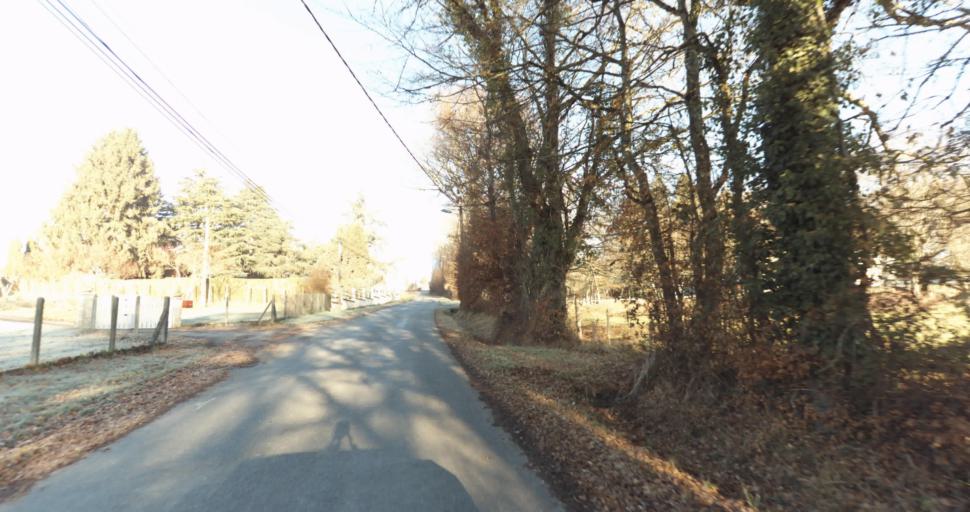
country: FR
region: Limousin
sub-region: Departement de la Haute-Vienne
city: Aixe-sur-Vienne
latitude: 45.8101
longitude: 1.1391
